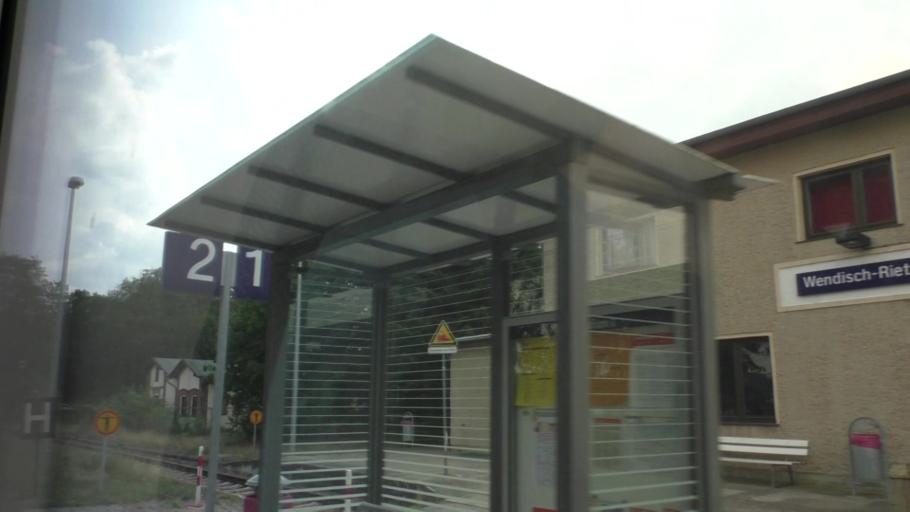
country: DE
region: Brandenburg
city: Wendisch Rietz
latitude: 52.2068
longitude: 14.0097
